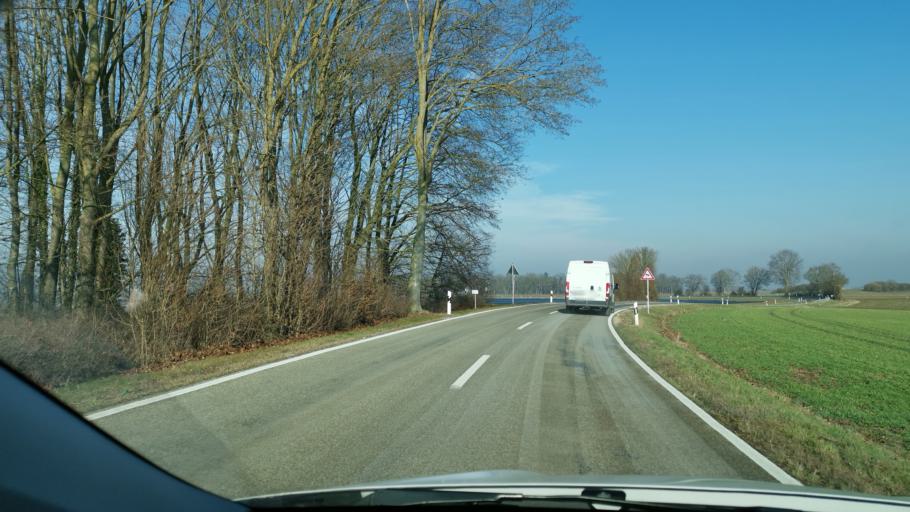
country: DE
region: Bavaria
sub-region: Swabia
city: Munster
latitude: 48.6341
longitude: 10.9254
